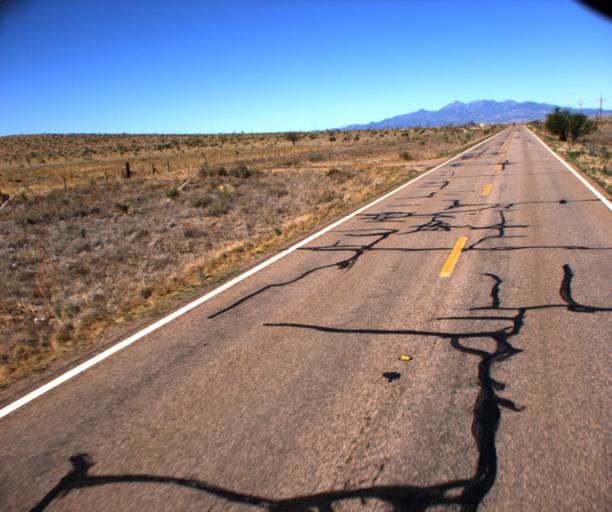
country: US
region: Arizona
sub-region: Cochise County
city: Huachuca City
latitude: 31.7240
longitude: -110.5093
